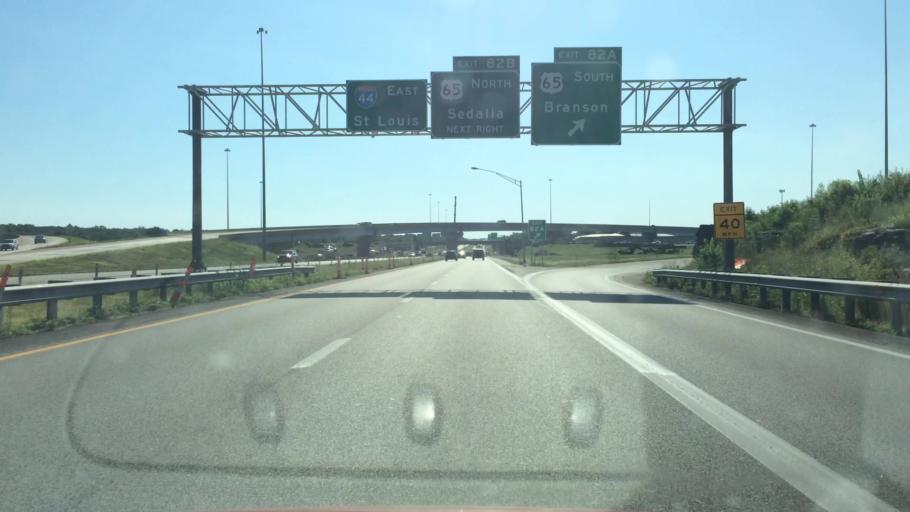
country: US
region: Missouri
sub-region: Greene County
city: Springfield
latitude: 37.2501
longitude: -93.2291
